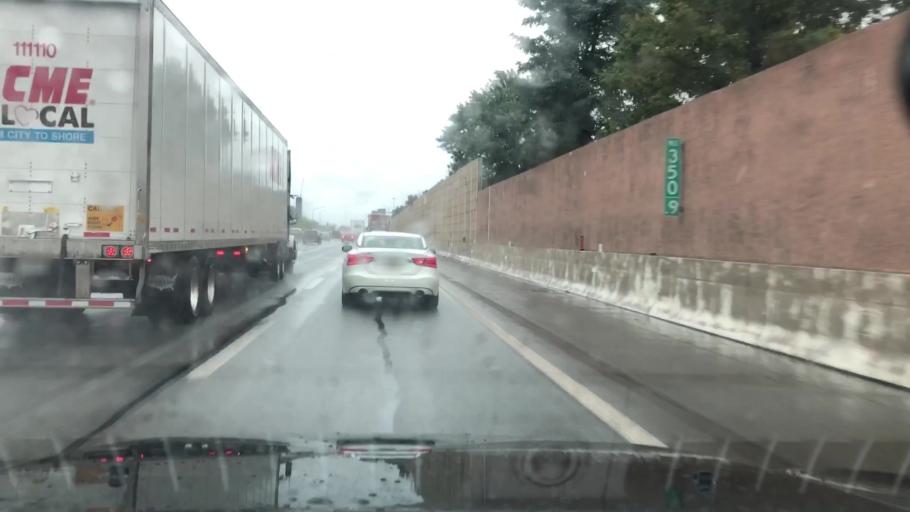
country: US
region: Pennsylvania
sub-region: Bucks County
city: Trevose
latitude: 40.1336
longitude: -74.9808
